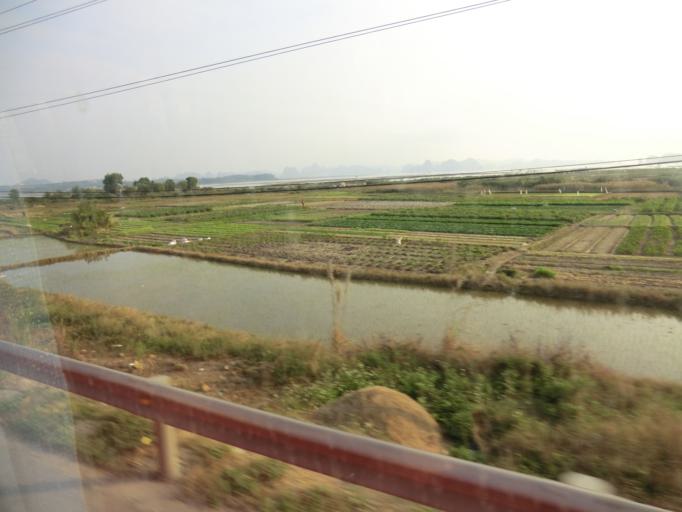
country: VN
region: Quang Ninh
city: Troi
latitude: 20.9560
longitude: 106.9665
